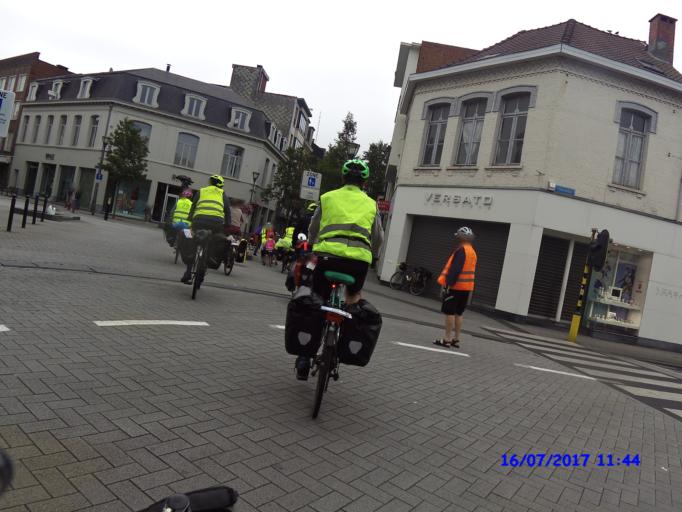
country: BE
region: Flanders
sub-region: Provincie Antwerpen
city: Turnhout
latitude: 51.3224
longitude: 4.9429
